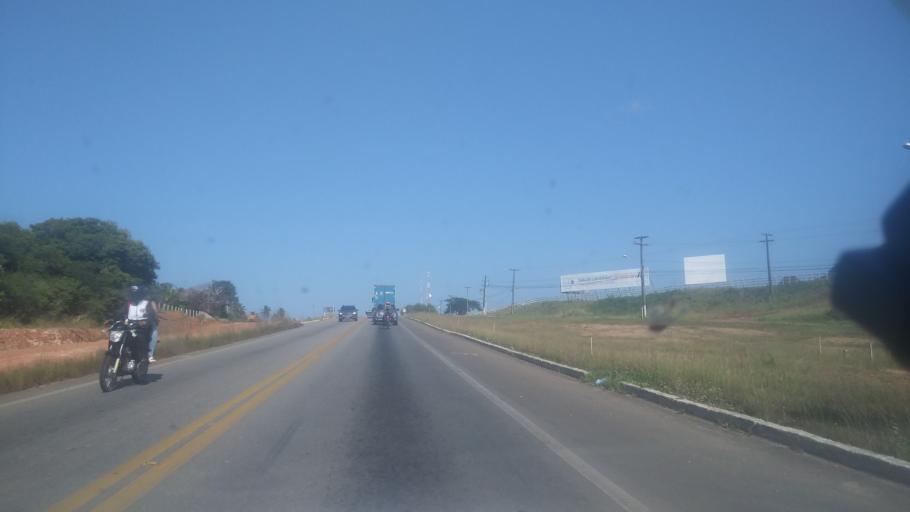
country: BR
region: Rio Grande do Norte
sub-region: Macaiba
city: Macaiba
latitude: -5.8671
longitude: -35.3663
